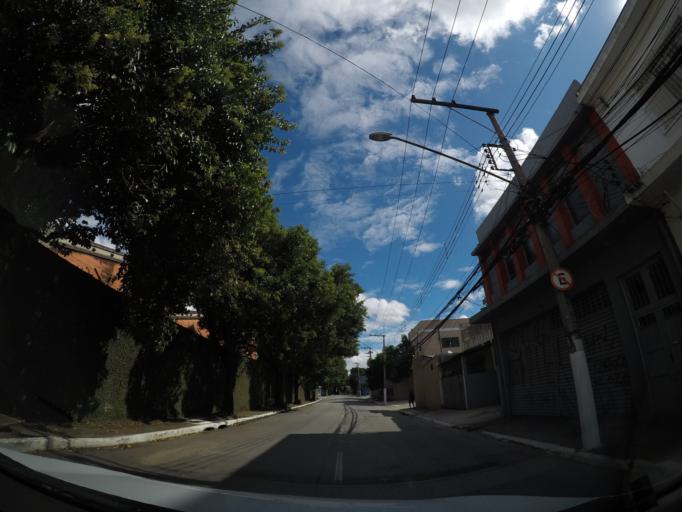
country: BR
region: Sao Paulo
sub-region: Guarulhos
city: Guarulhos
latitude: -23.4899
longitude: -46.5541
